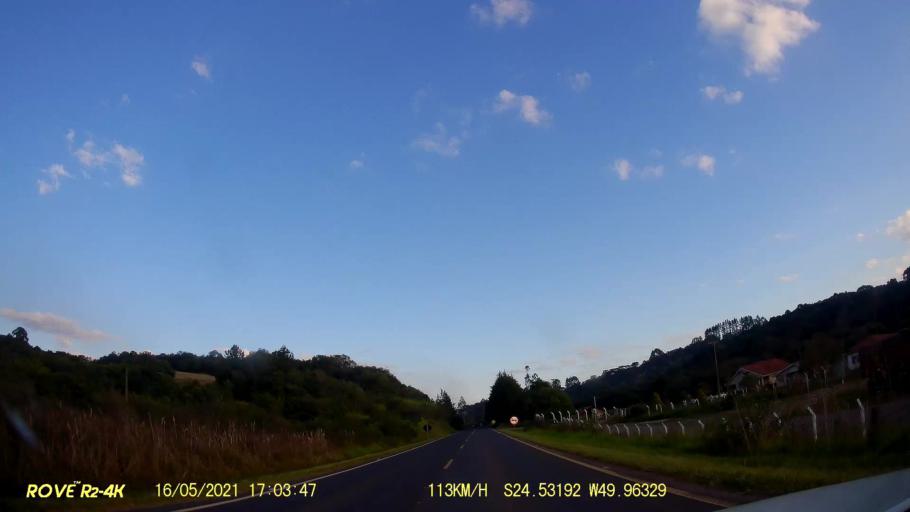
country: BR
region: Parana
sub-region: Pirai Do Sul
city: Pirai do Sul
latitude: -24.5319
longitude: -49.9633
